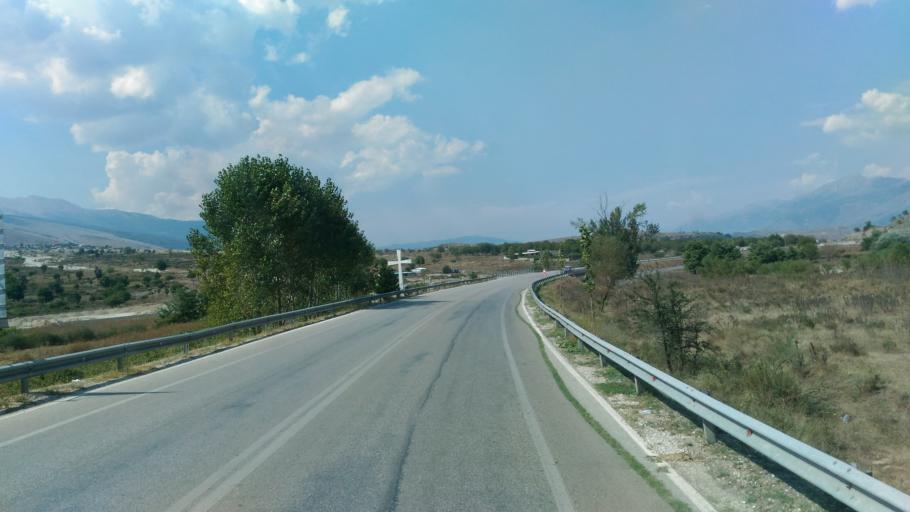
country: AL
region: Gjirokaster
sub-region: Rrethi i Gjirokastres
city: Dervician
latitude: 40.0388
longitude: 20.1772
